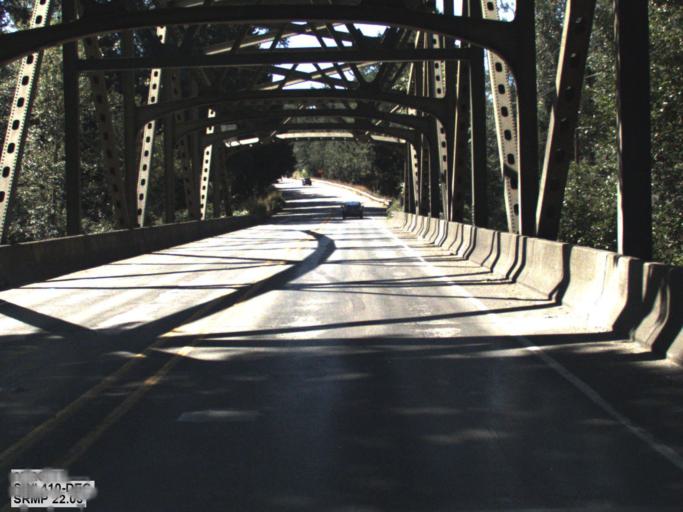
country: US
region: Washington
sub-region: Pierce County
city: Buckley
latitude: 47.1742
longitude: -122.0232
